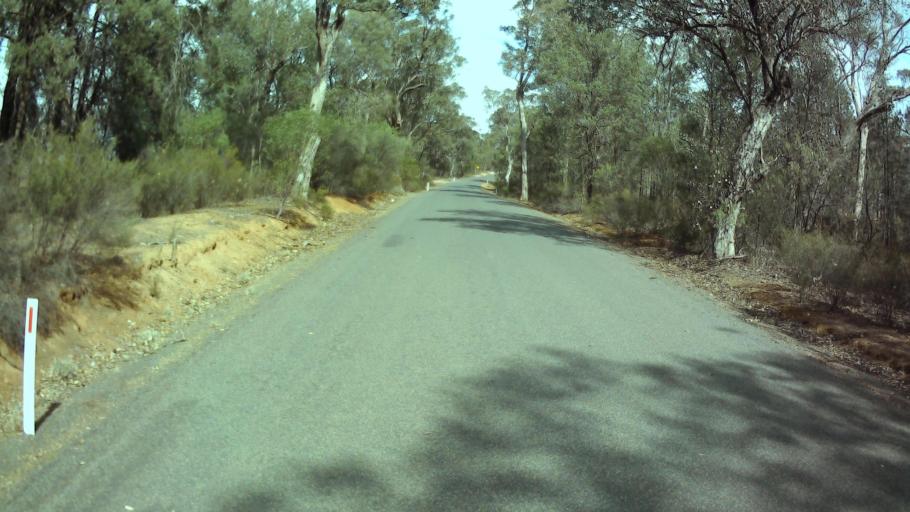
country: AU
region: New South Wales
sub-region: Weddin
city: Grenfell
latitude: -33.8049
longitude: 148.0342
